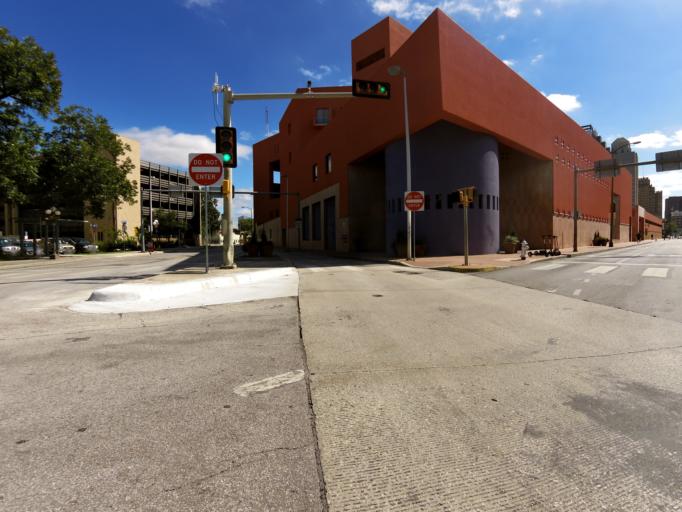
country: US
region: Texas
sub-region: Bexar County
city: San Antonio
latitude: 29.4330
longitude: -98.4934
